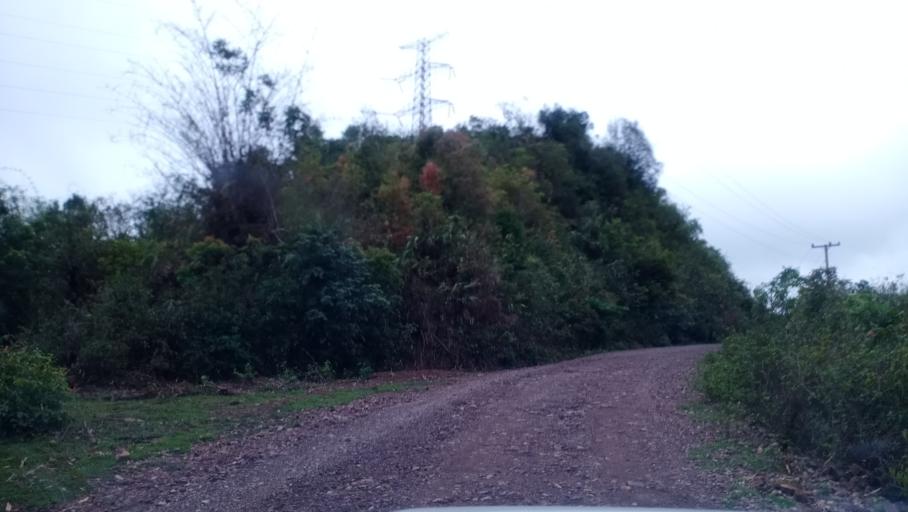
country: LA
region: Phongsali
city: Phongsali
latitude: 21.3417
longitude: 102.0854
